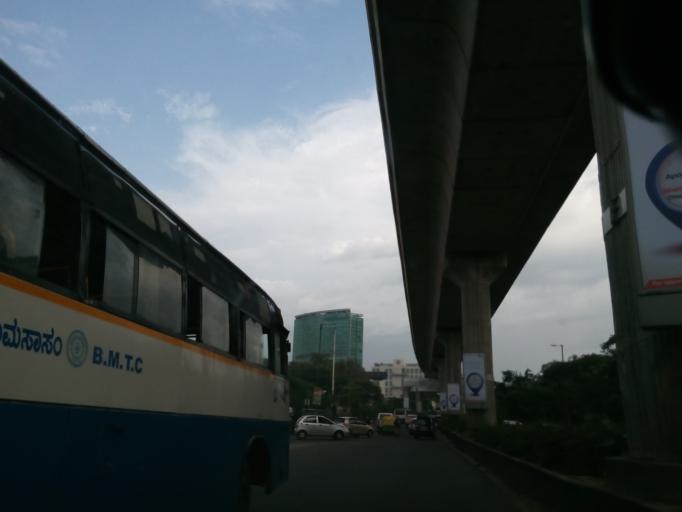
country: IN
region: Karnataka
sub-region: Bangalore Urban
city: Bangalore
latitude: 13.0181
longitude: 77.5535
